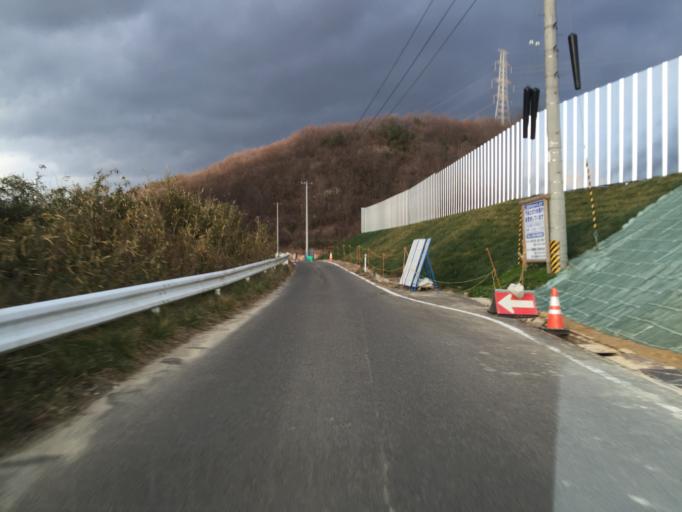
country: JP
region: Fukushima
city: Motomiya
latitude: 37.5273
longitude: 140.4152
